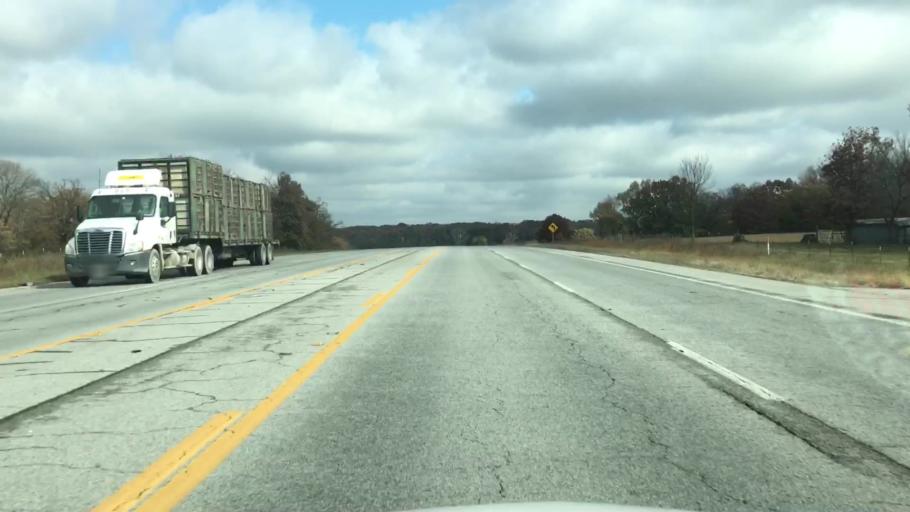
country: US
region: Arkansas
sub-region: Benton County
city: Gentry
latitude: 36.2339
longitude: -94.4911
